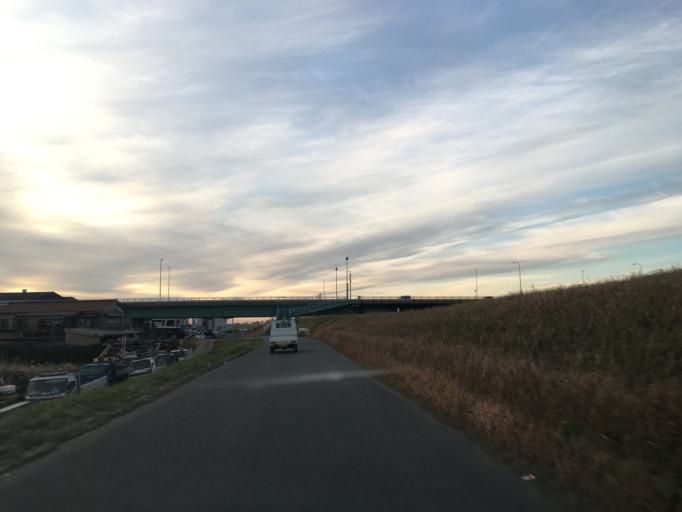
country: JP
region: Chiba
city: Katori-shi
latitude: 35.9059
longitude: 140.4922
